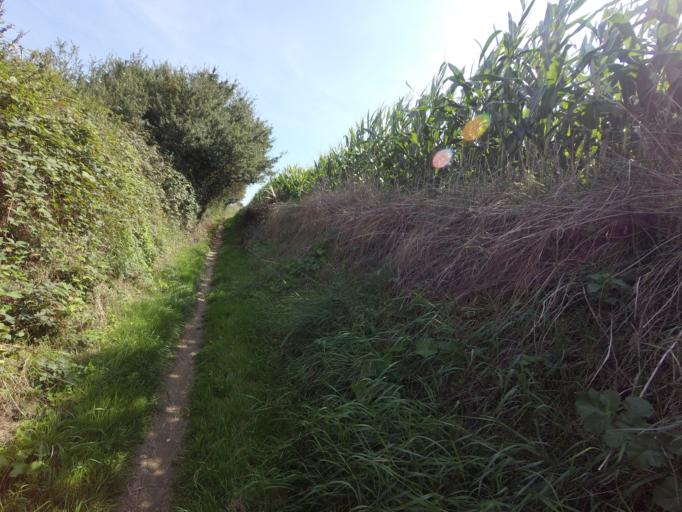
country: NL
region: Limburg
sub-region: Valkenburg aan de Geul
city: Schin op Geul
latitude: 50.8401
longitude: 5.8956
